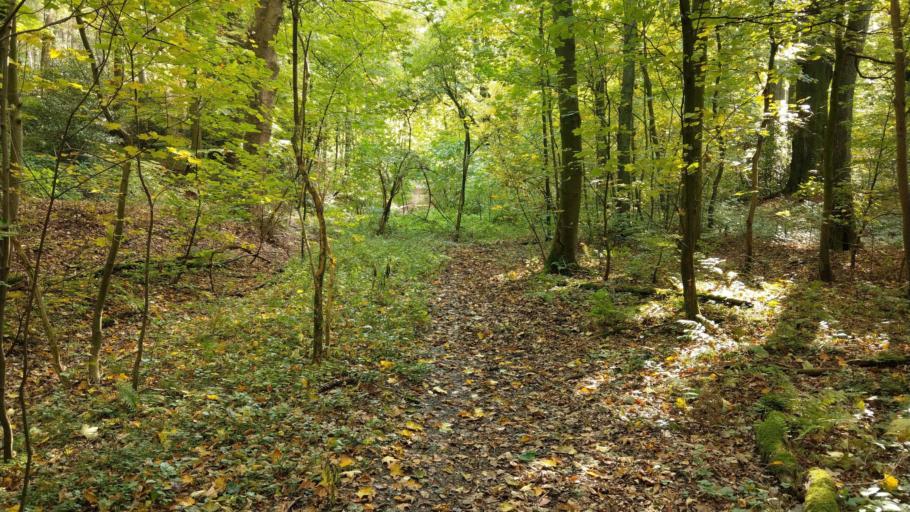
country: NL
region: Limburg
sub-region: Gemeente Vaals
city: Vaals
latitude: 50.7533
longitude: 6.0388
